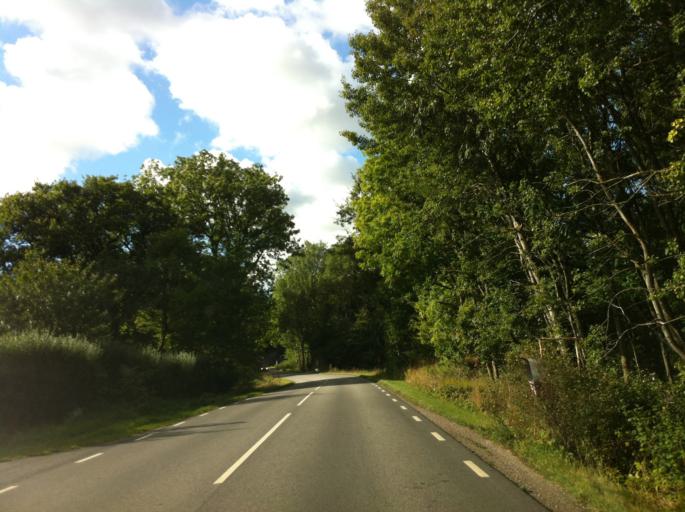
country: SE
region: Skane
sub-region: Tomelilla Kommun
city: Tomelilla
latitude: 55.6516
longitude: 13.9446
